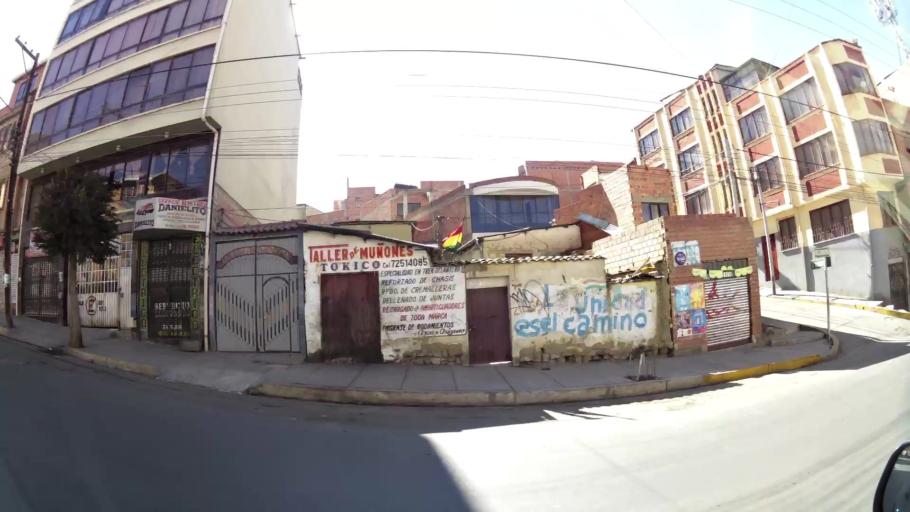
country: BO
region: La Paz
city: La Paz
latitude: -16.5105
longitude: -68.1374
